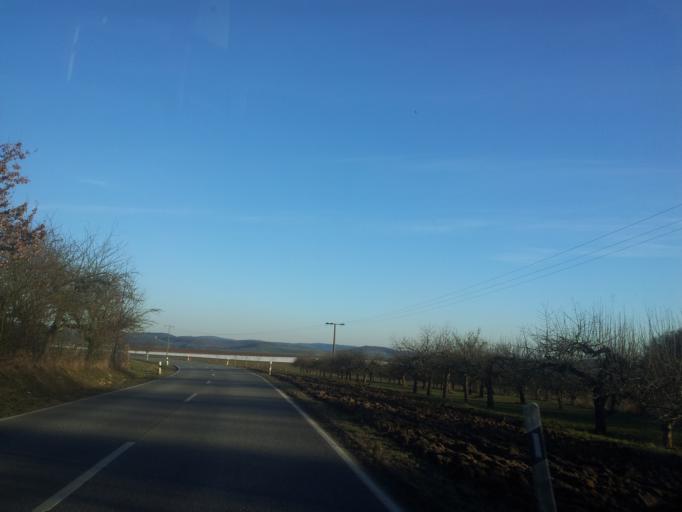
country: DE
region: Baden-Wuerttemberg
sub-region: Regierungsbezirk Stuttgart
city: Untergruppenbach
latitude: 49.0867
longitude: 9.2476
